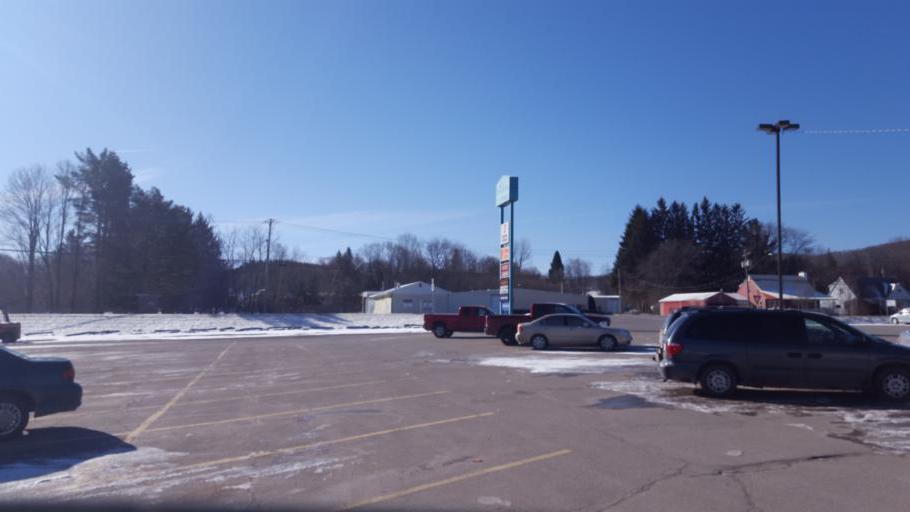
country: US
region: New York
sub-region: Allegany County
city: Wellsville
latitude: 42.1275
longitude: -77.9663
